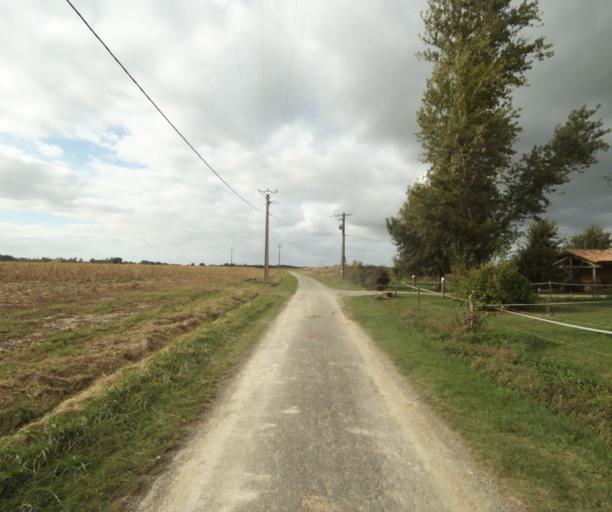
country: FR
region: Midi-Pyrenees
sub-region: Departement du Tarn-et-Garonne
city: Finhan
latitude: 43.8939
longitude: 1.1073
